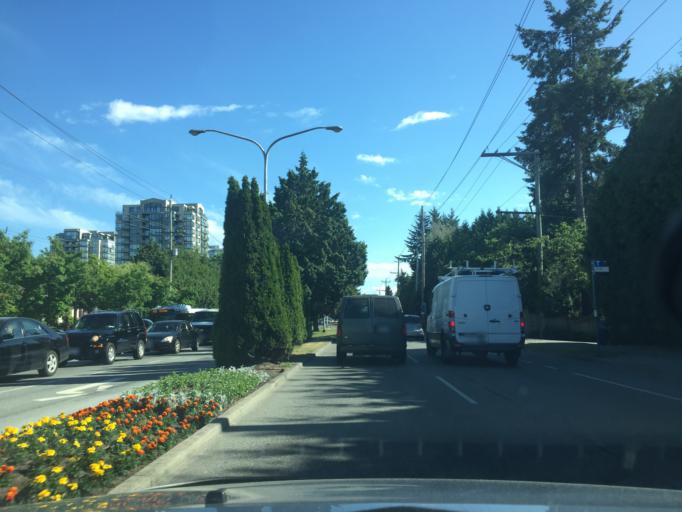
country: CA
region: British Columbia
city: Richmond
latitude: 49.1700
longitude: -123.1247
